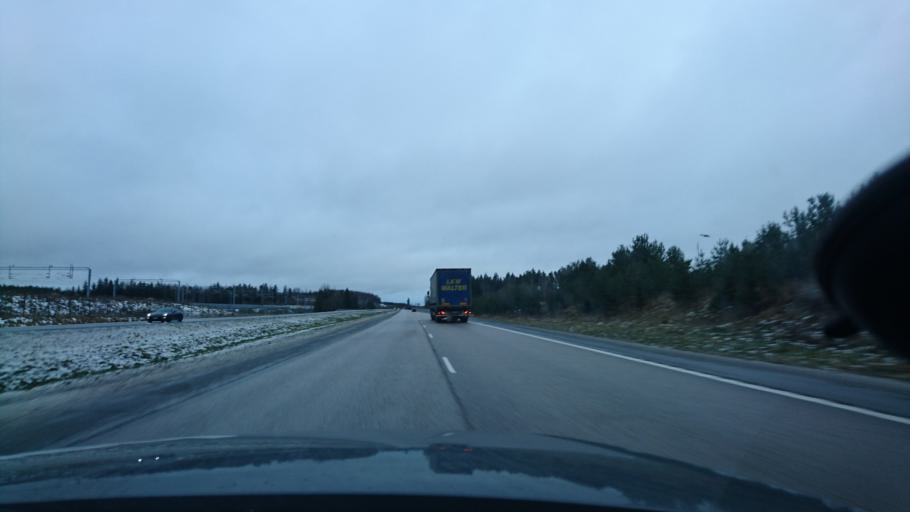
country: FI
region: Uusimaa
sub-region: Helsinki
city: Maentsaelae
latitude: 60.6475
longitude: 25.3099
